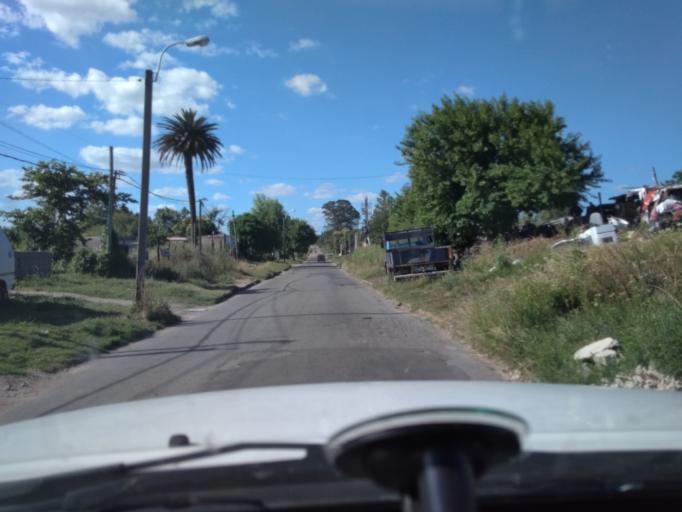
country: UY
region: Canelones
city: La Paz
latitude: -34.8087
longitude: -56.2093
